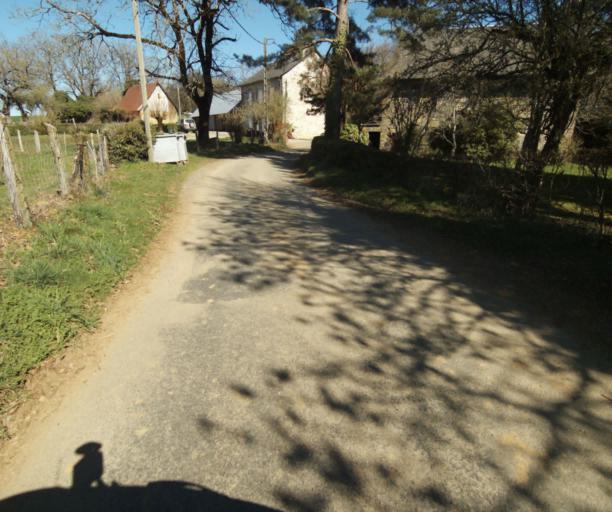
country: FR
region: Limousin
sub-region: Departement de la Correze
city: Seilhac
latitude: 45.3501
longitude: 1.7290
